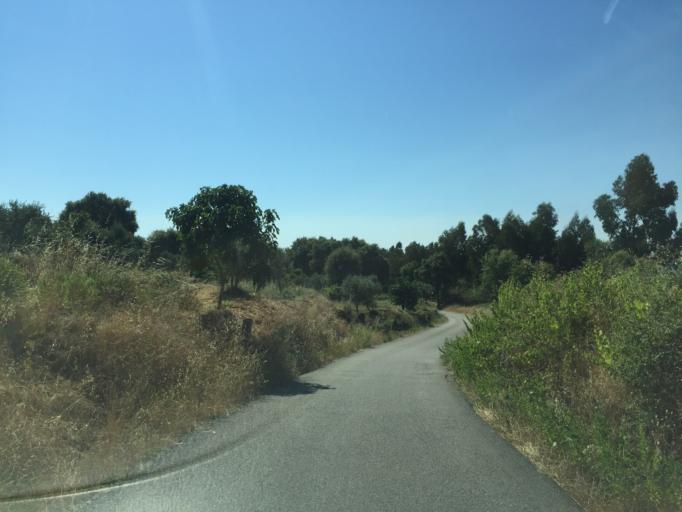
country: PT
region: Santarem
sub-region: Ferreira do Zezere
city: Ferreira do Zezere
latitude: 39.5931
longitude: -8.2872
